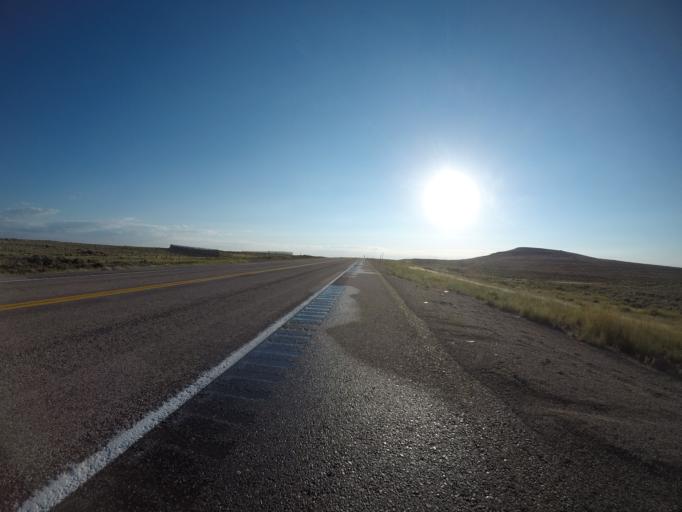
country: US
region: Wyoming
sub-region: Lincoln County
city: Kemmerer
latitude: 41.8862
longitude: -110.4237
